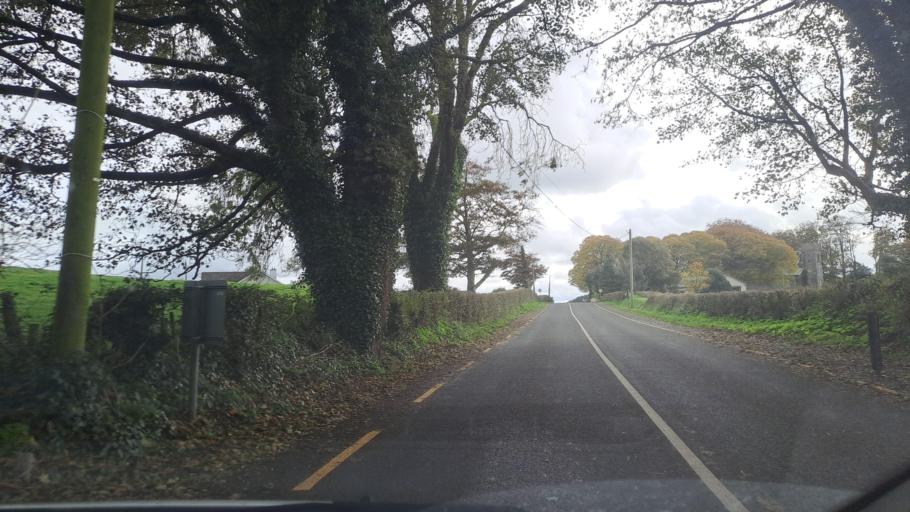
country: IE
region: Ulster
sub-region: An Cabhan
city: Mullagh
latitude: 53.8163
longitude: -6.9660
